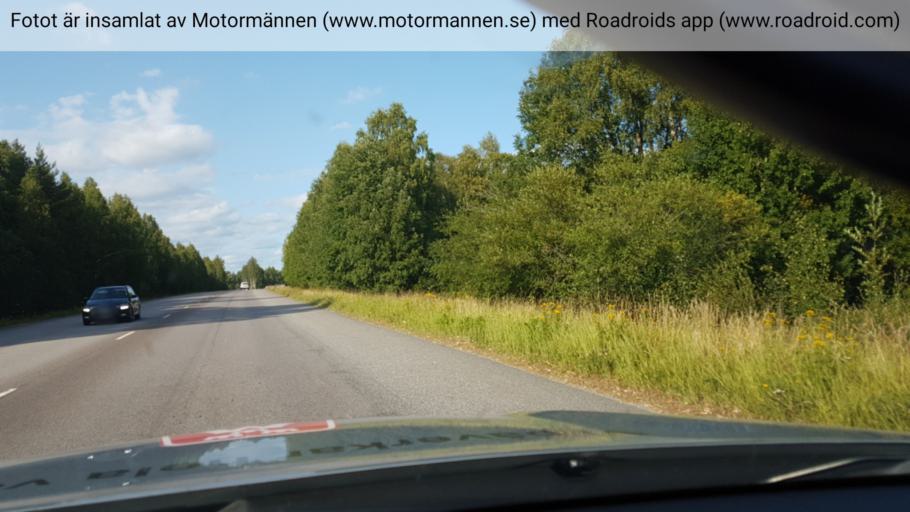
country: SE
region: Norrbotten
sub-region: Pitea Kommun
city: Pitea
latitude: 65.2872
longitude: 21.5072
